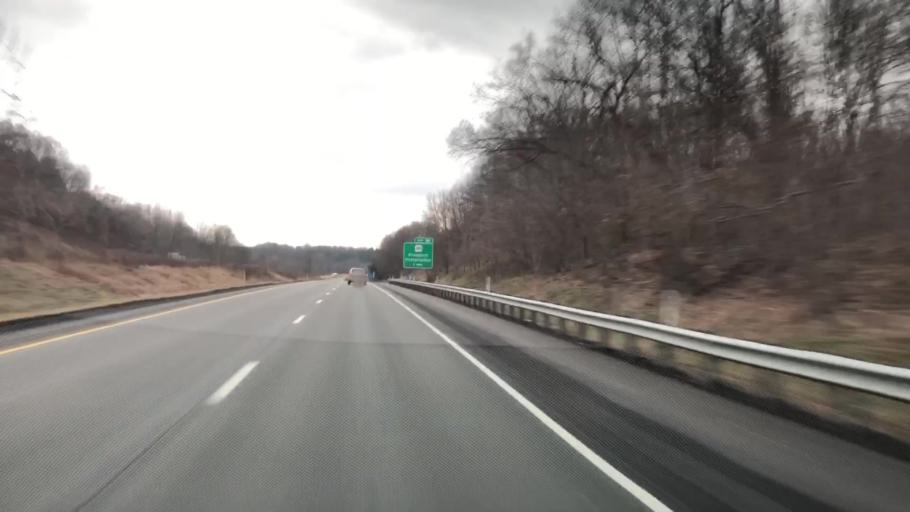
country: US
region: Pennsylvania
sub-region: Butler County
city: Prospect
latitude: 40.9370
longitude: -80.1344
